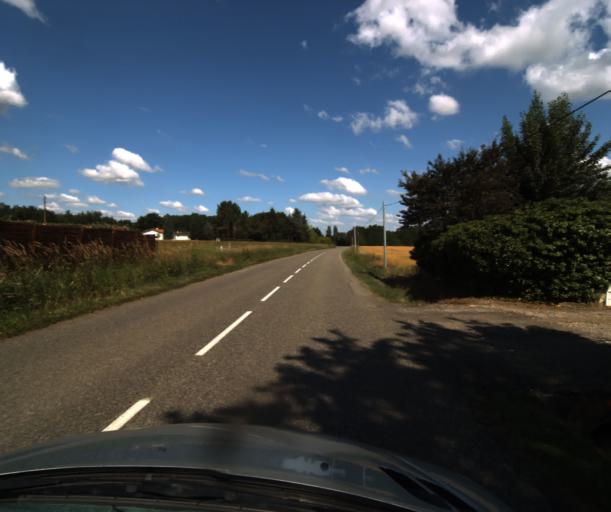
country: FR
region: Midi-Pyrenees
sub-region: Departement du Tarn-et-Garonne
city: Campsas
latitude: 43.9087
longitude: 1.2865
